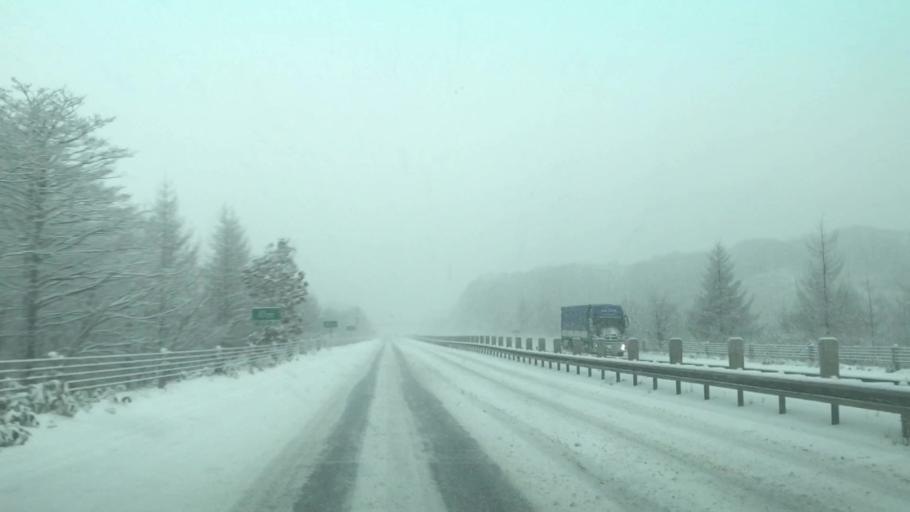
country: JP
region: Hokkaido
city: Muroran
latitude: 42.4348
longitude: 141.1237
